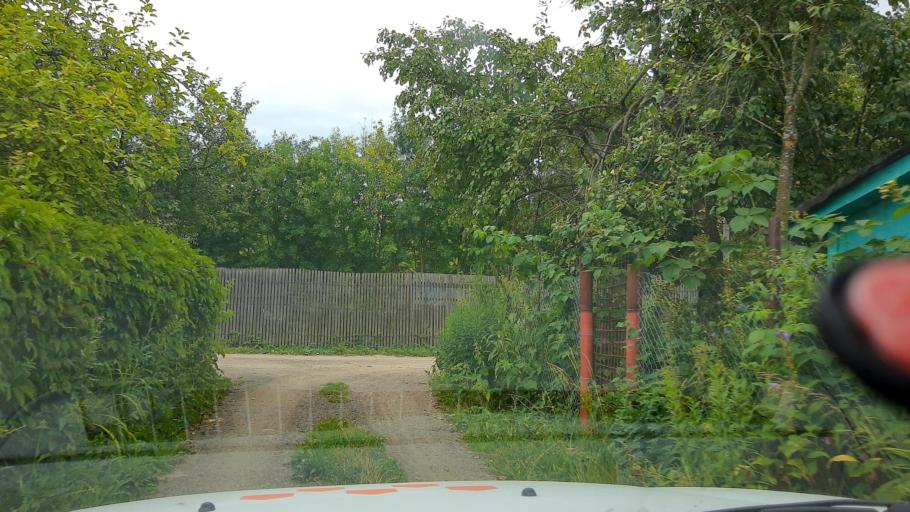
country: RU
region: Nizjnij Novgorod
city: Gorbatovka
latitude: 56.2436
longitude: 43.8225
